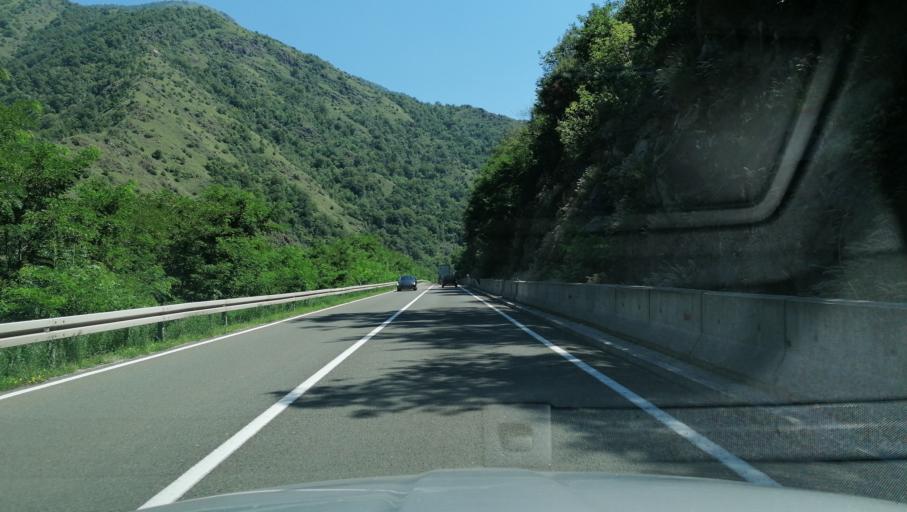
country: RS
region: Central Serbia
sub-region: Raski Okrug
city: Kraljevo
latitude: 43.5885
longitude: 20.5760
